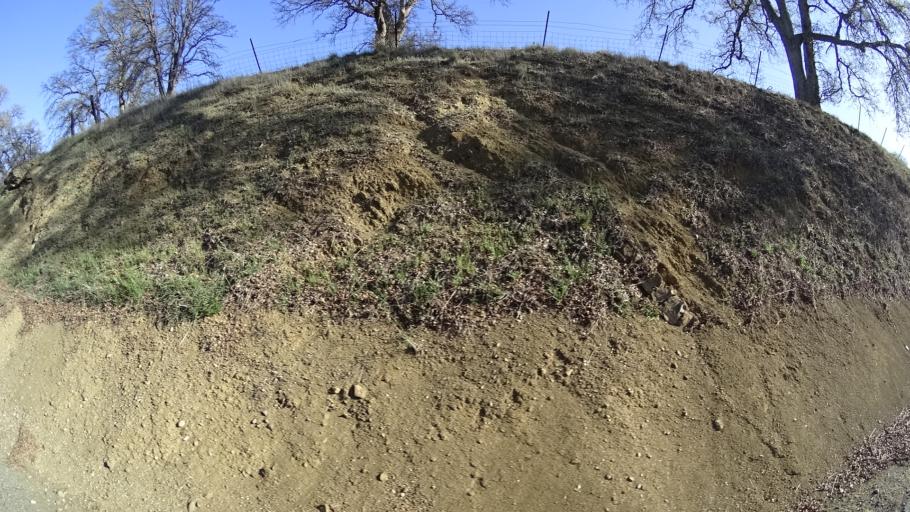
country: US
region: California
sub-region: Tehama County
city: Rancho Tehama Reserve
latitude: 39.7898
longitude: -122.5085
